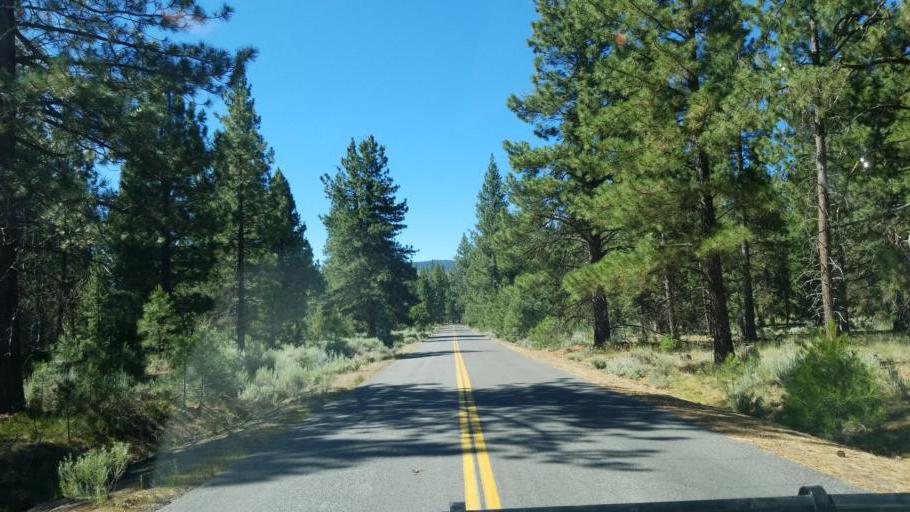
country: US
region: California
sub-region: Lassen County
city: Susanville
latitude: 40.5531
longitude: -120.7772
